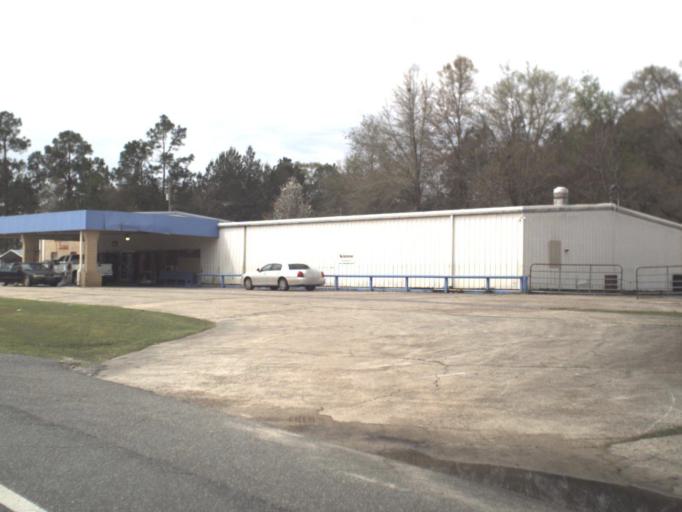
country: US
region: Florida
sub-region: Calhoun County
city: Blountstown
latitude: 30.5362
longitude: -85.1918
